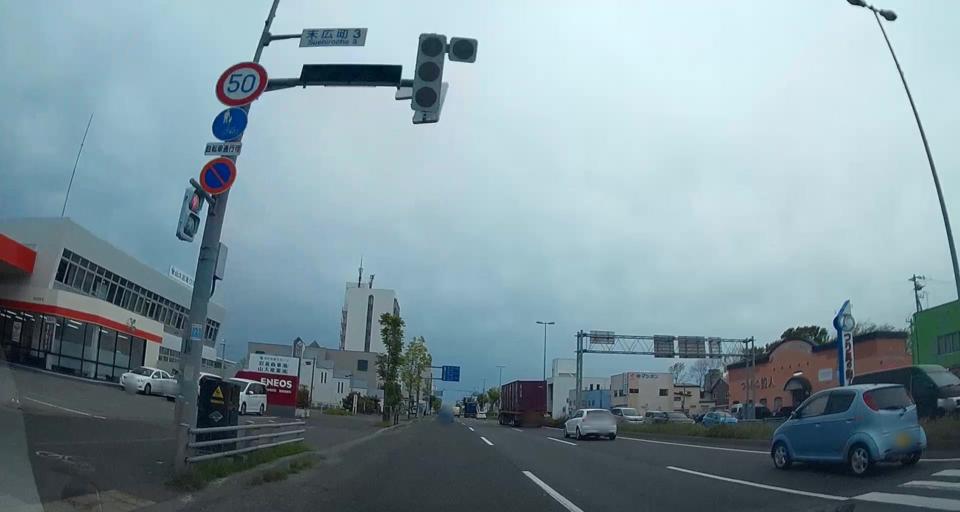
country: JP
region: Hokkaido
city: Tomakomai
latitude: 42.6389
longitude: 141.6117
